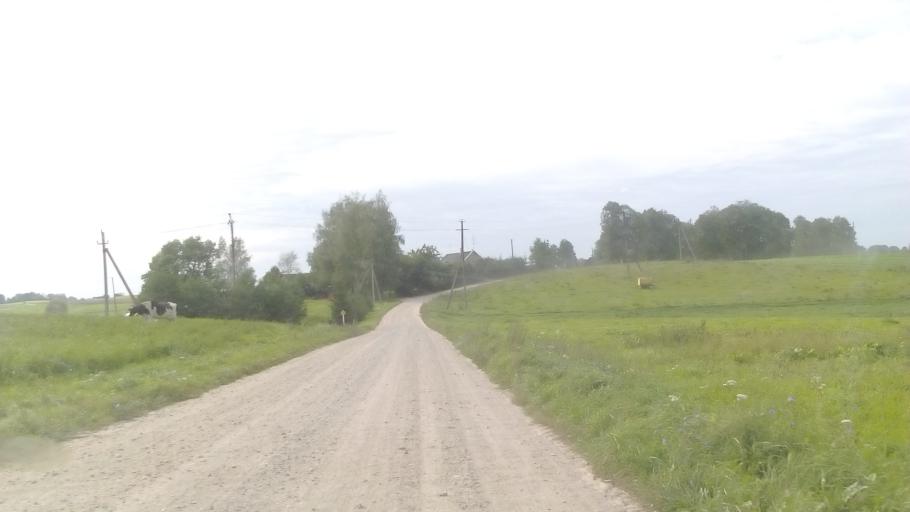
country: LT
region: Alytaus apskritis
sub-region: Alytus
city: Alytus
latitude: 54.3303
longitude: 23.8877
